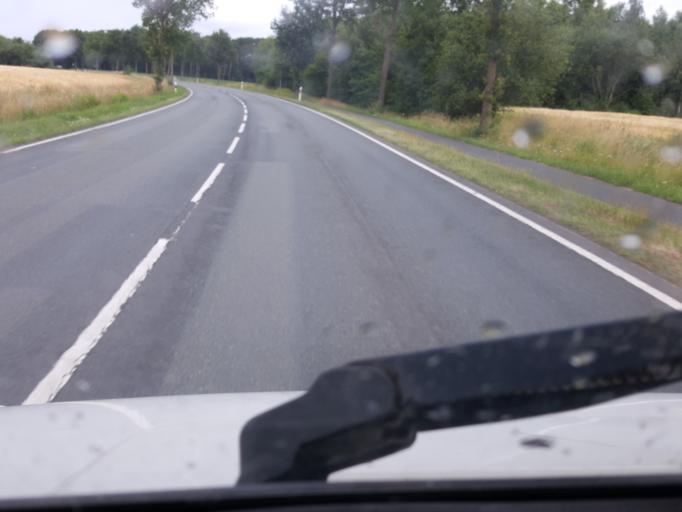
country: DE
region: Lower Saxony
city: Raddestorf
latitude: 52.4392
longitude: 8.9384
